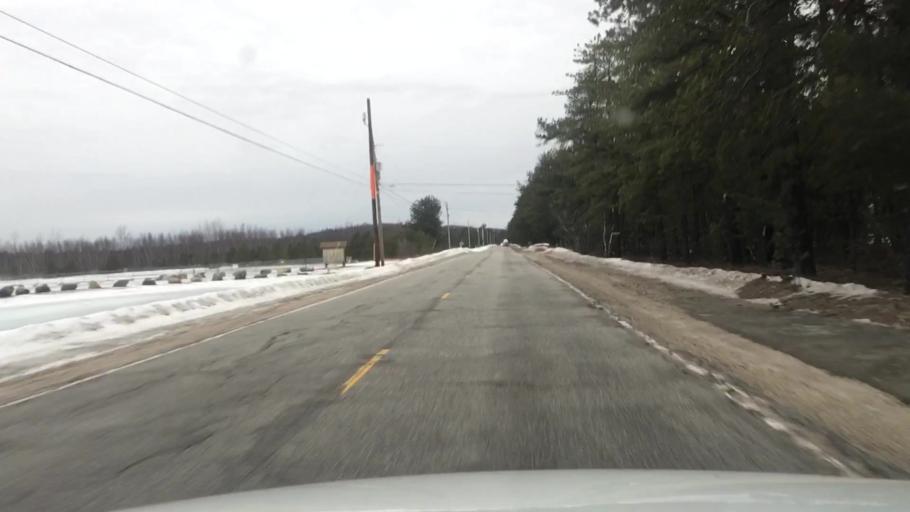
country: US
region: Maine
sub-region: York County
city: Shapleigh
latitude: 43.5877
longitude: -70.8761
